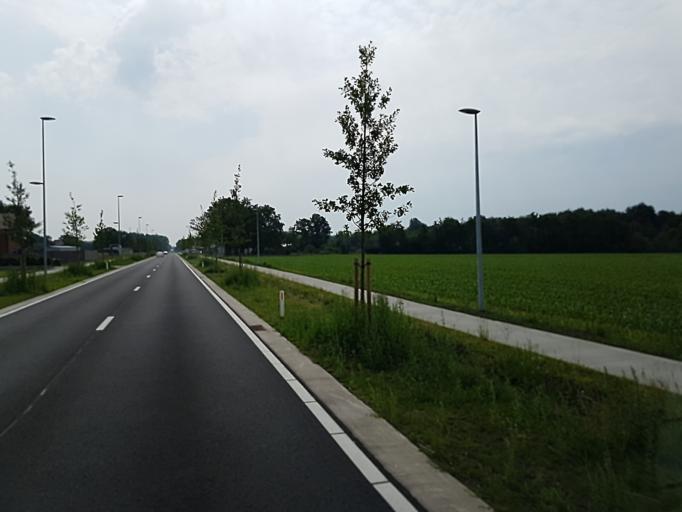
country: BE
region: Flanders
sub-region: Provincie Limburg
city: Leopoldsburg
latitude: 51.1445
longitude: 5.2198
